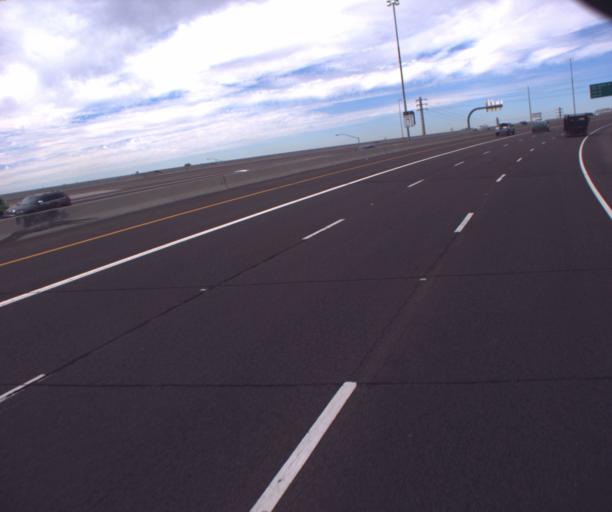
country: US
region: Arizona
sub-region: Maricopa County
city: Tempe Junction
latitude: 33.4392
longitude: -111.9656
